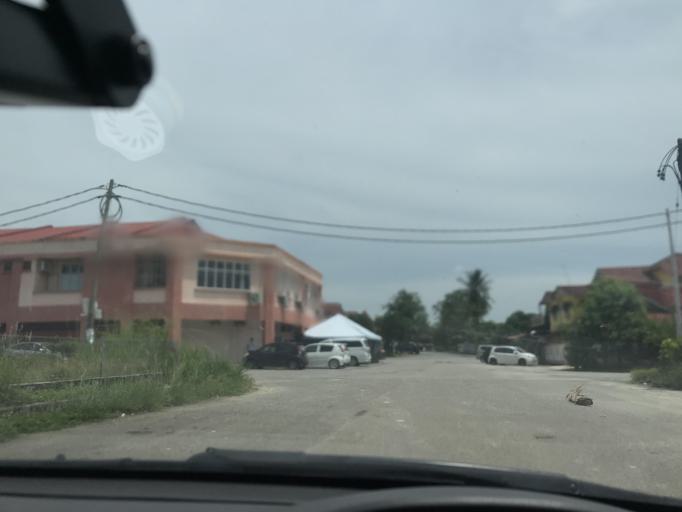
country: MY
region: Kelantan
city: Kota Bharu
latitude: 6.1210
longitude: 102.2185
